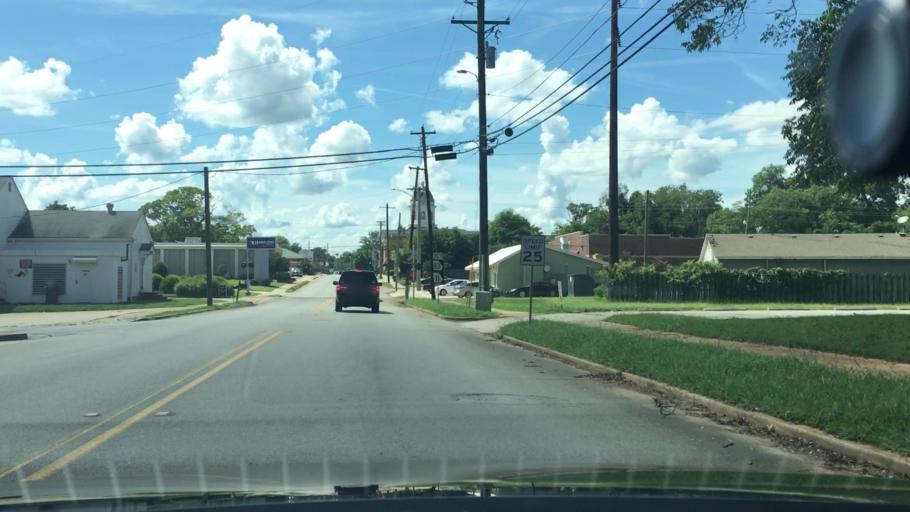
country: US
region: Georgia
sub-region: Jasper County
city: Monticello
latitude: 33.3036
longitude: -83.6809
